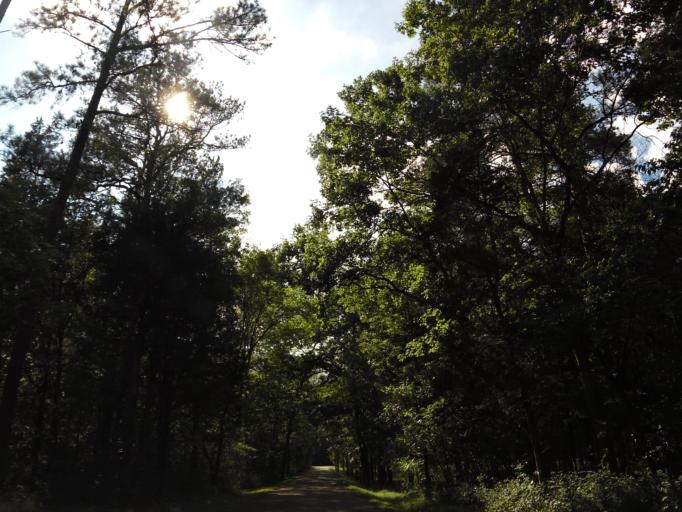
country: US
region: Georgia
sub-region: Walker County
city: Chickamauga
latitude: 34.9047
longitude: -85.2688
